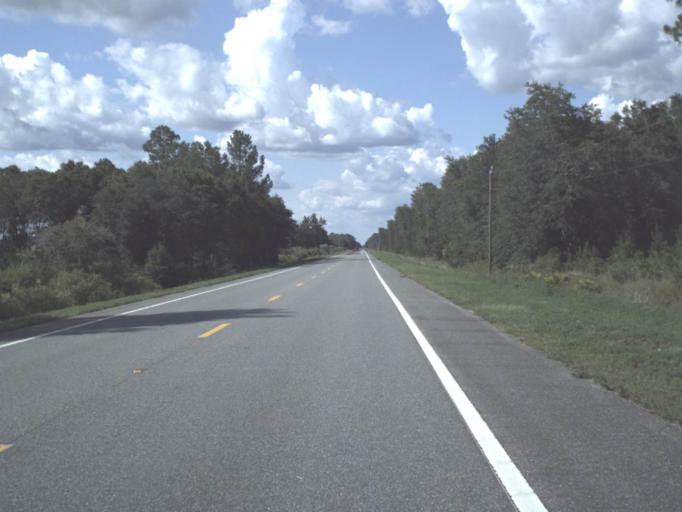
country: US
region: Florida
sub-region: Taylor County
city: Steinhatchee
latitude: 29.7981
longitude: -83.3201
